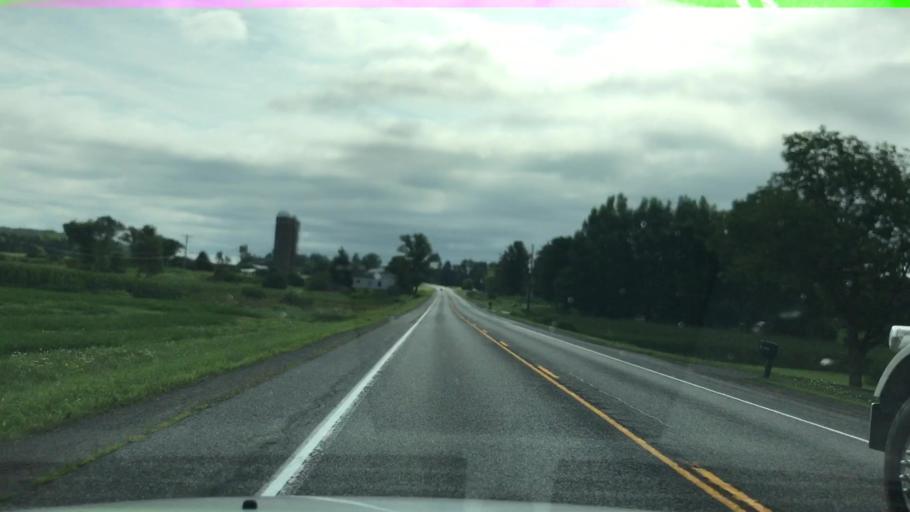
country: US
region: New York
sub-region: Erie County
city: Alden
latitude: 42.8354
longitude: -78.4131
